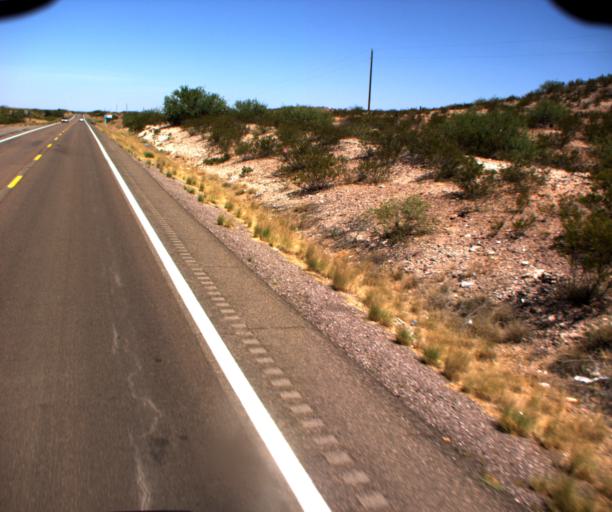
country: US
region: Arizona
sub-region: Graham County
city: Bylas
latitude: 33.1973
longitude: -110.1824
